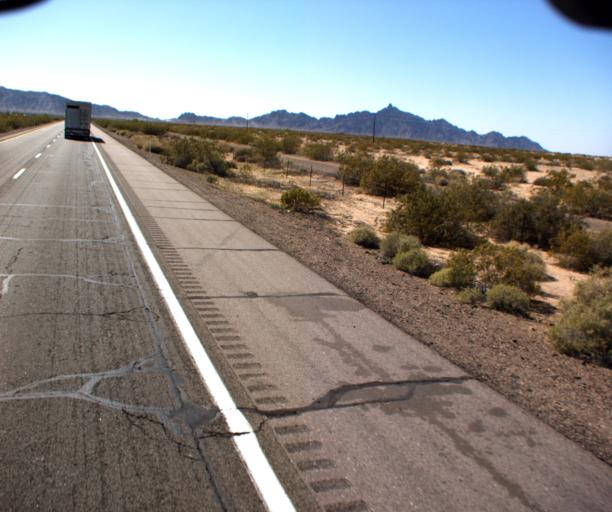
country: US
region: Arizona
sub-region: Yuma County
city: Wellton
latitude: 32.7467
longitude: -113.6732
